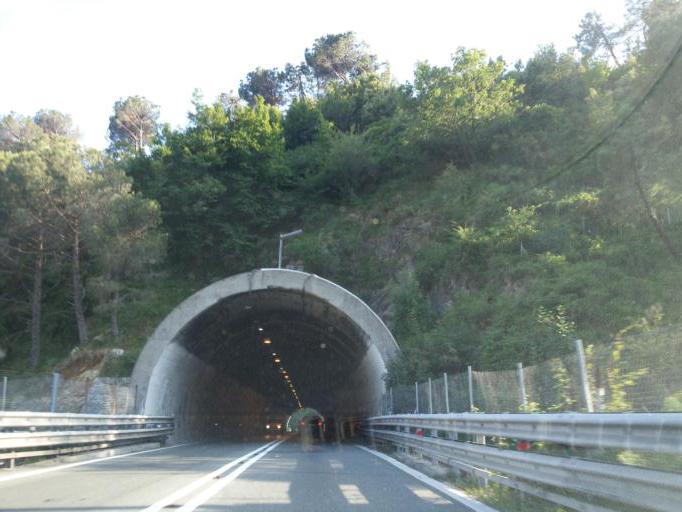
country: IT
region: Liguria
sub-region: Provincia di Genova
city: Genoa
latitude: 44.4361
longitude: 8.9421
